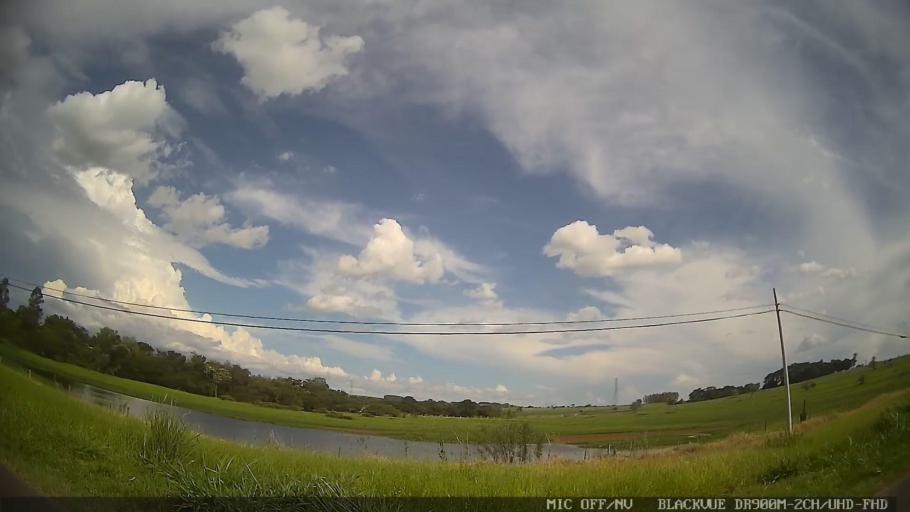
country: BR
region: Sao Paulo
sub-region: Conchas
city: Conchas
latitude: -23.0571
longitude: -47.9629
